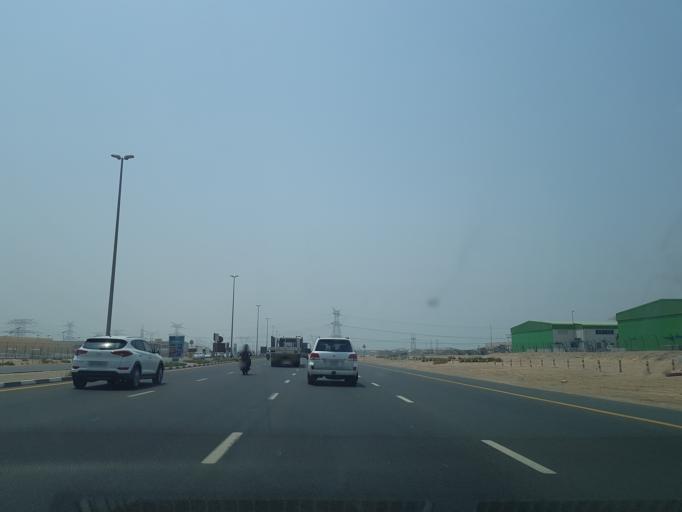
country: AE
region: Ash Shariqah
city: Sharjah
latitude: 25.1632
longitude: 55.3862
